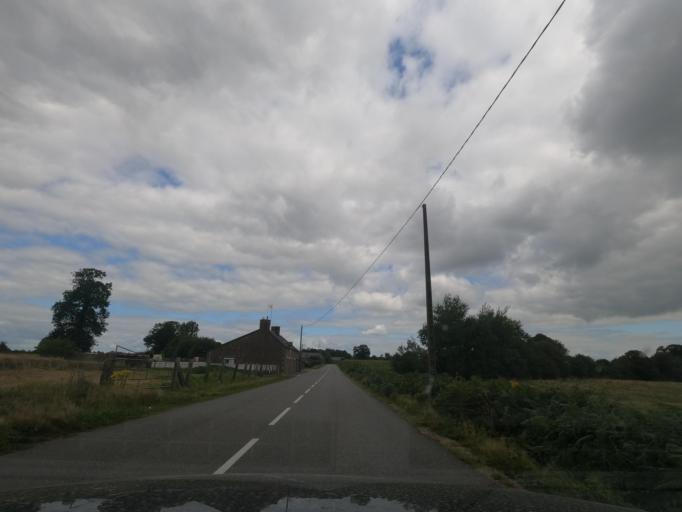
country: FR
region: Brittany
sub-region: Departement d'Ille-et-Vilaine
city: Landean
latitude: 48.4308
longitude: -1.1147
